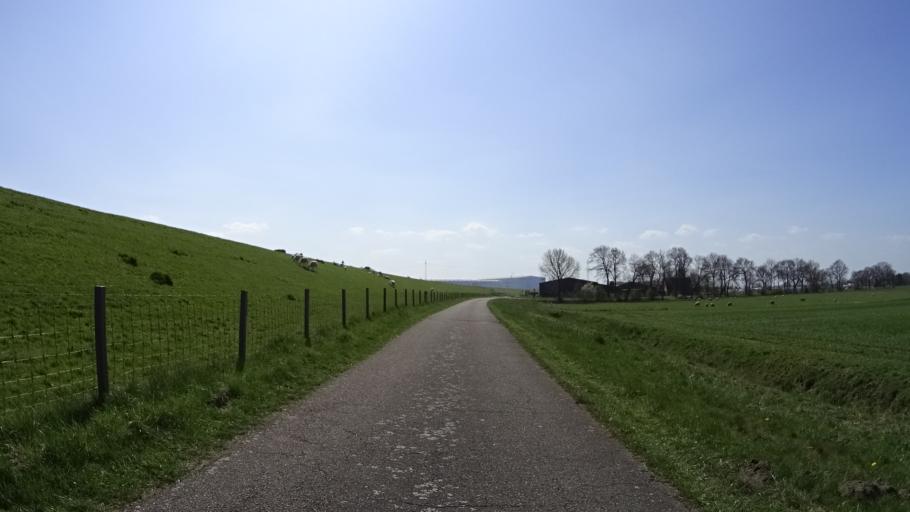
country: DE
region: Lower Saxony
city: Papenburg
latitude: 53.1160
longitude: 7.3709
